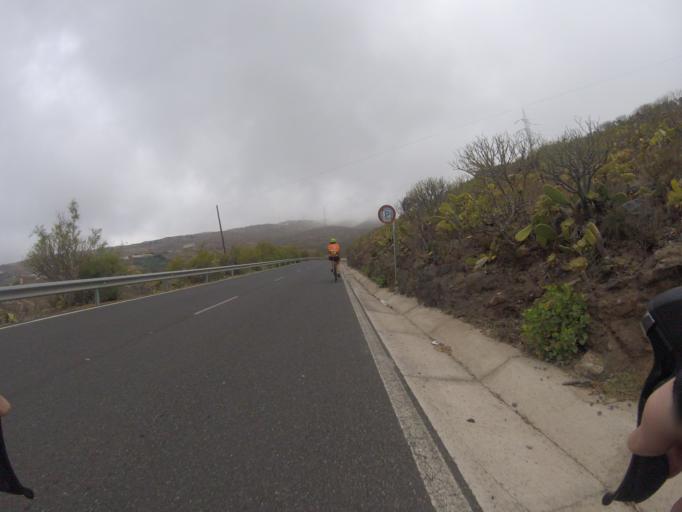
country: ES
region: Canary Islands
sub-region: Provincia de Santa Cruz de Tenerife
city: Guimar
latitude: 28.2893
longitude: -16.4025
